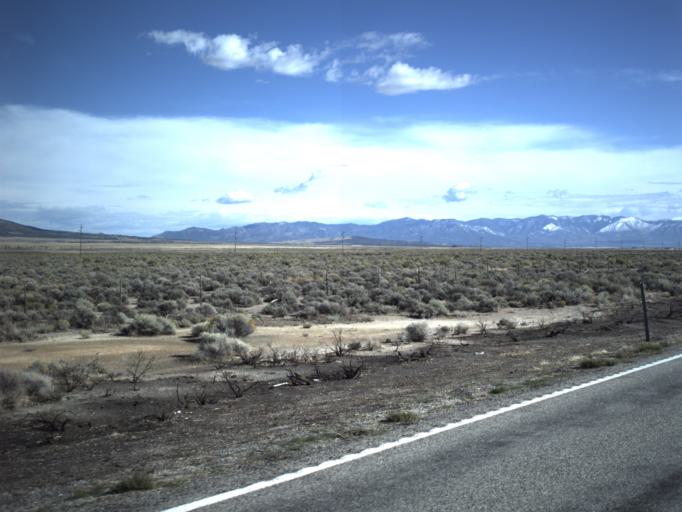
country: US
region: Utah
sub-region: Millard County
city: Delta
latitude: 39.2747
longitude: -112.4566
